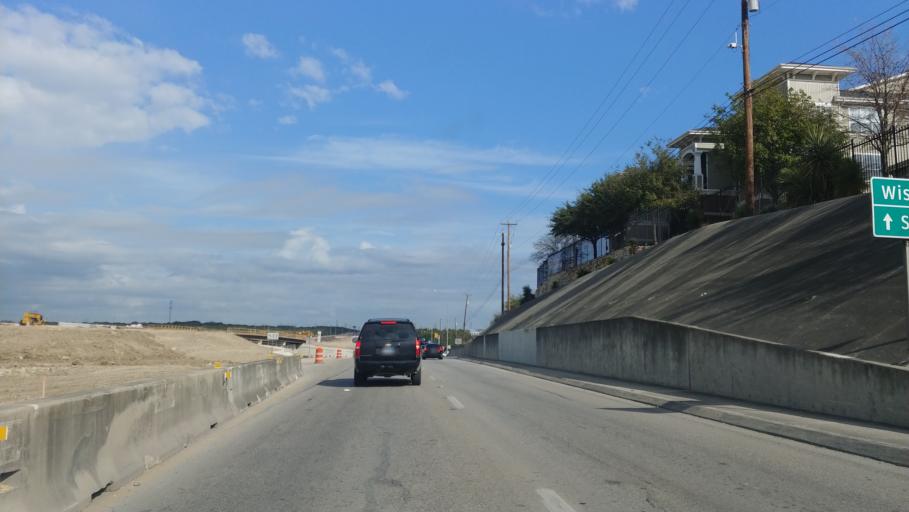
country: US
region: Texas
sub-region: Bexar County
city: Leon Valley
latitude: 29.4632
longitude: -98.7109
